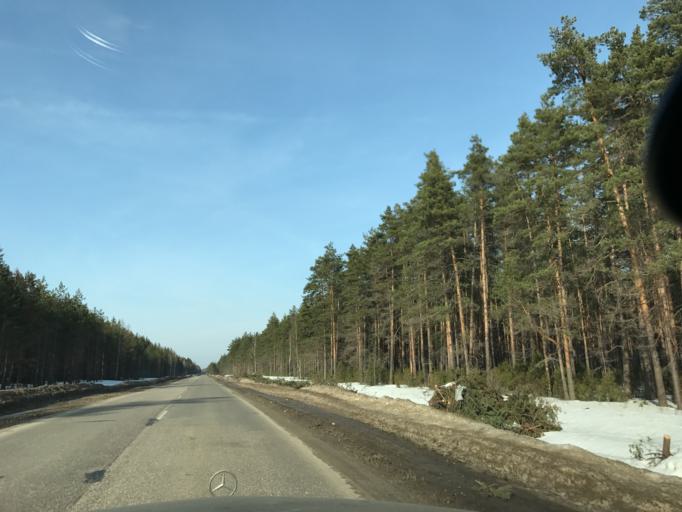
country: RU
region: Vladimir
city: Galitsy
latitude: 56.0405
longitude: 42.8629
